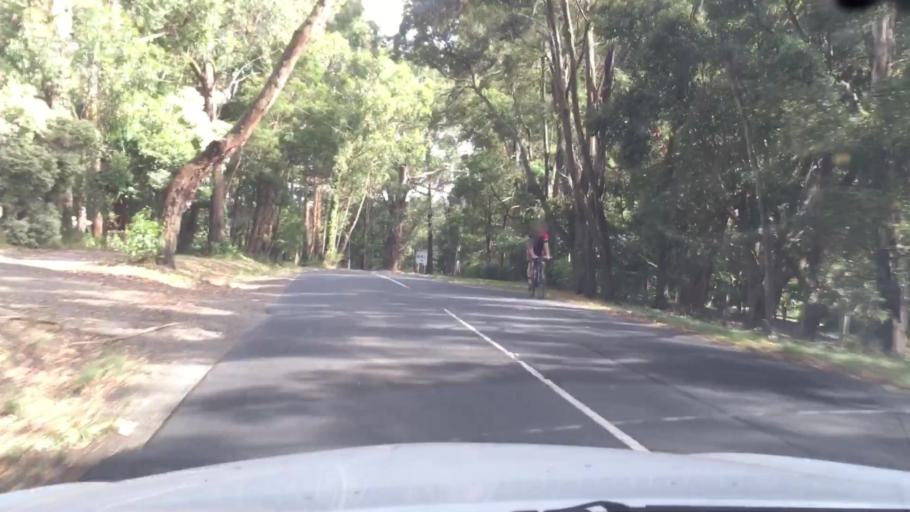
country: AU
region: Victoria
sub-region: Yarra Ranges
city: Macclesfield
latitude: -37.8932
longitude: 145.4754
